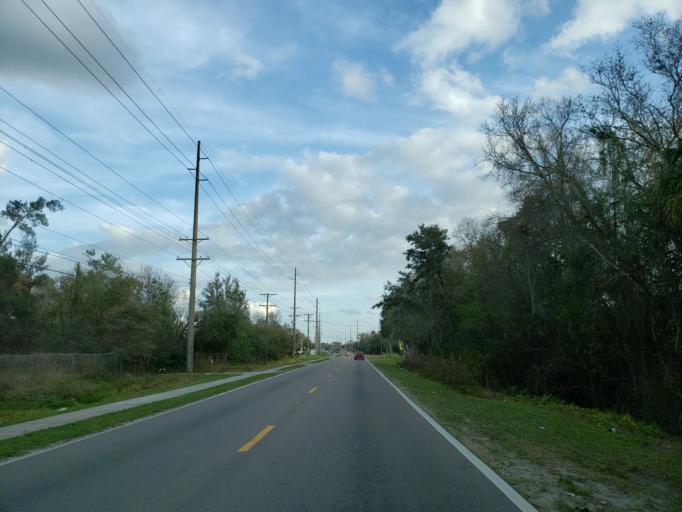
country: US
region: Florida
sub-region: Hillsborough County
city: Riverview
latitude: 27.8244
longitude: -82.3003
